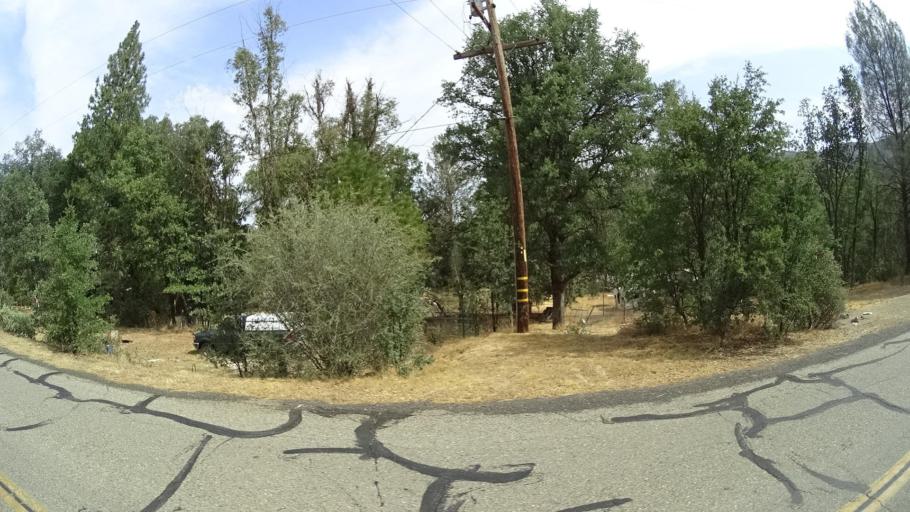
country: US
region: California
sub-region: Mariposa County
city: Midpines
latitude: 37.5636
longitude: -119.9442
